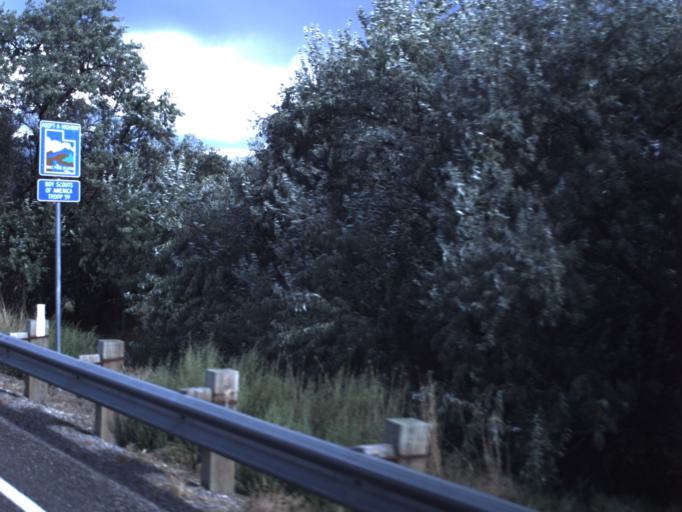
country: US
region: Utah
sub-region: Cache County
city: Lewiston
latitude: 41.9754
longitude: -111.9387
